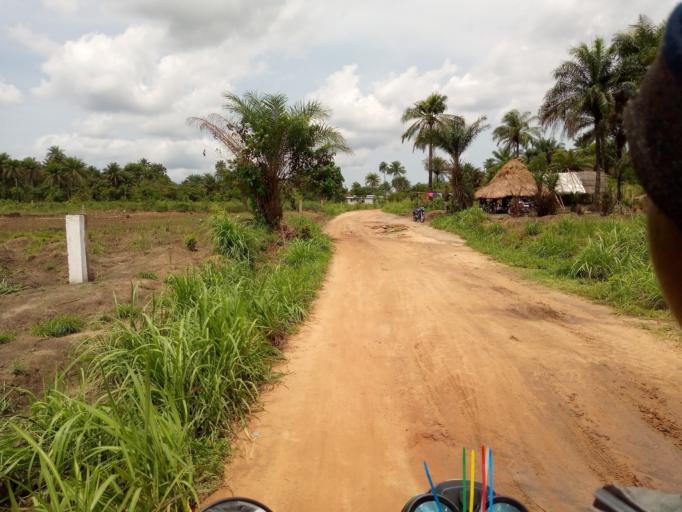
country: SL
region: Western Area
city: Waterloo
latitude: 8.3214
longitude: -12.9409
